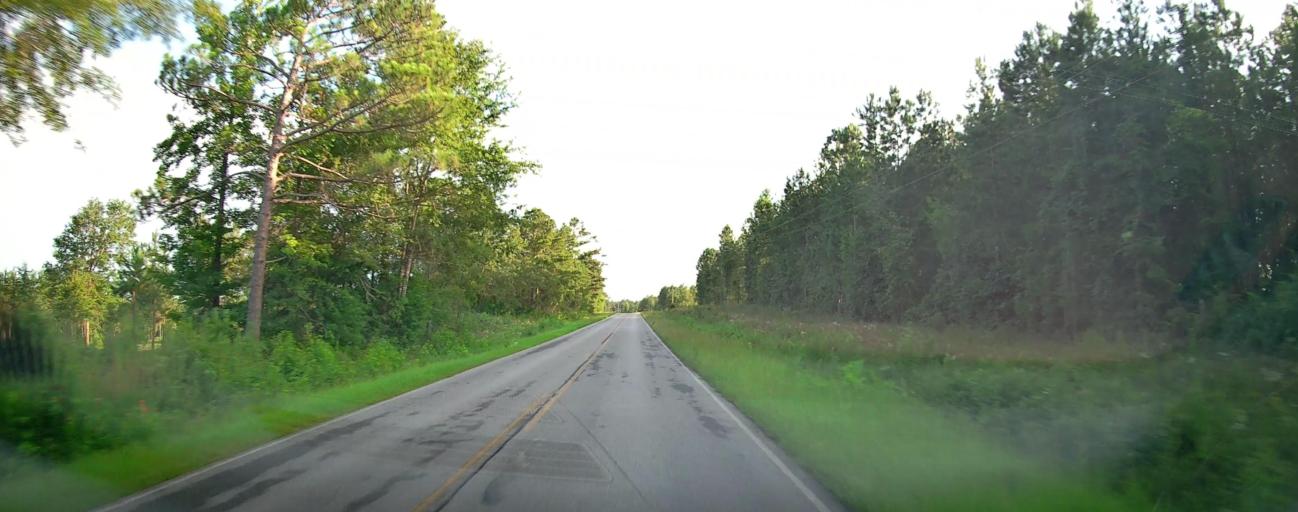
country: US
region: Georgia
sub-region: Bibb County
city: West Point
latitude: 32.7069
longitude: -83.8481
